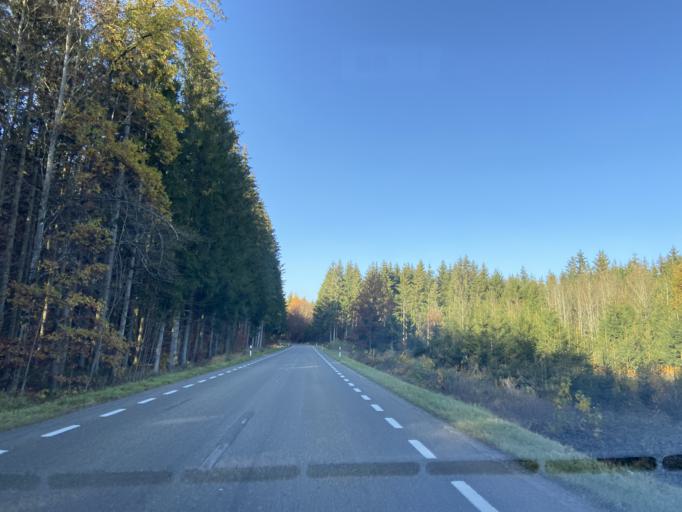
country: DE
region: Baden-Wuerttemberg
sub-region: Tuebingen Region
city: Sigmaringendorf
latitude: 48.0526
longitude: 9.2682
